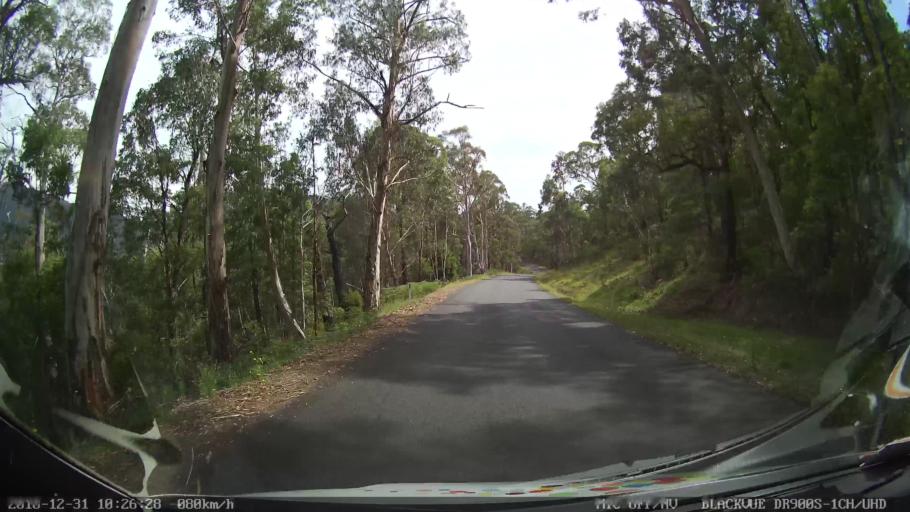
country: AU
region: New South Wales
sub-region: Snowy River
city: Jindabyne
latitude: -36.4952
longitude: 148.1400
